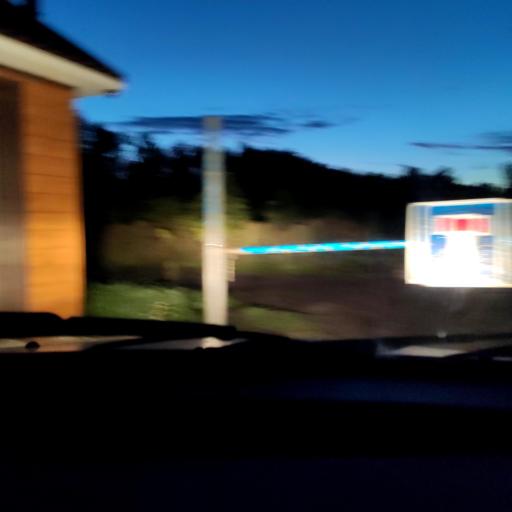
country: RU
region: Bashkortostan
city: Mikhaylovka
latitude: 54.8094
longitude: 55.9366
